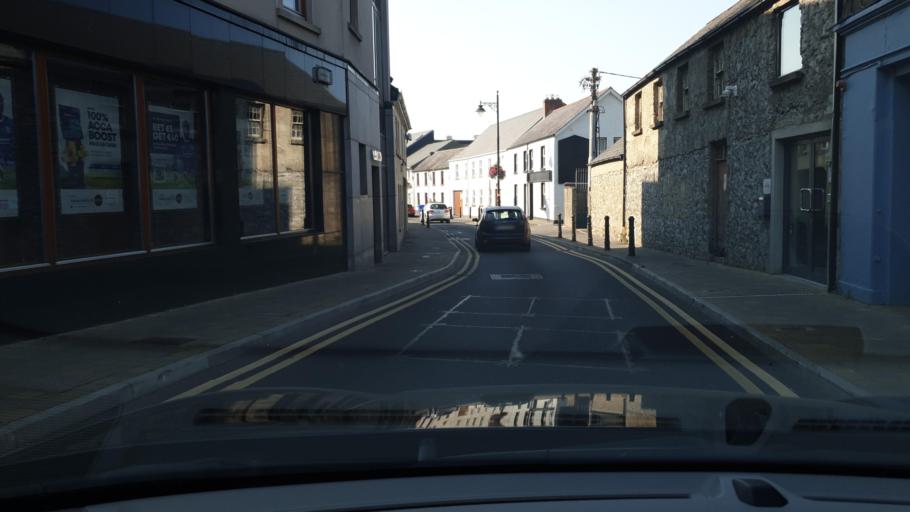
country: IE
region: Leinster
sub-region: An Mhi
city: Navan
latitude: 53.6520
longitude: -6.6881
